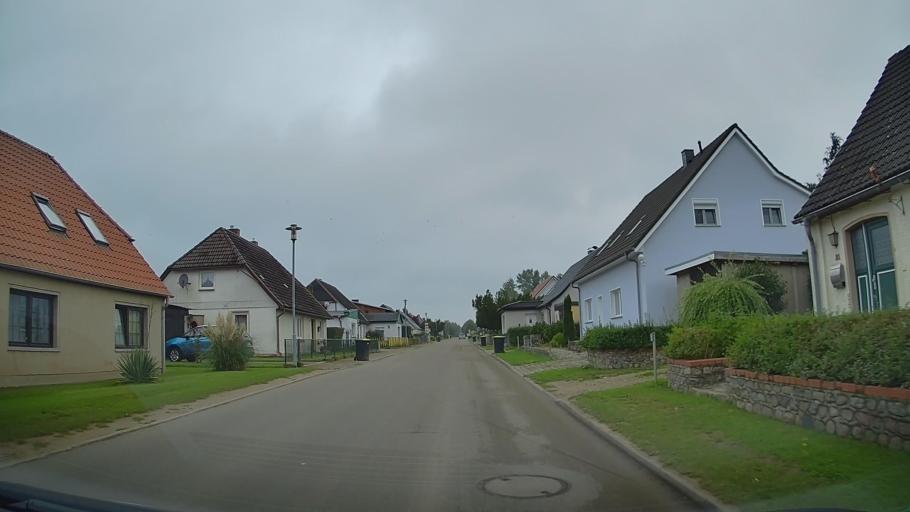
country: DE
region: Mecklenburg-Vorpommern
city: Blowatz
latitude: 53.9793
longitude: 11.5515
